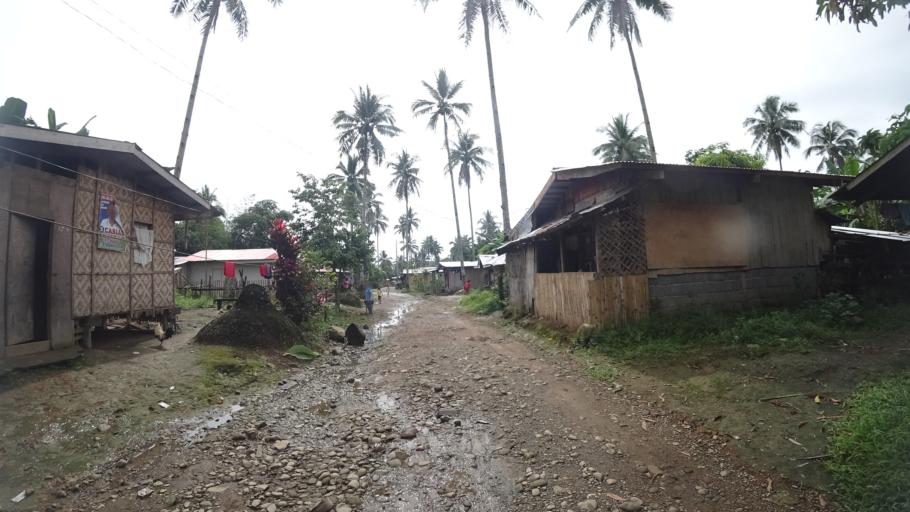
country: PH
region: Eastern Visayas
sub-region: Province of Leyte
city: Bugho
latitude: 10.8303
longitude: 124.8893
